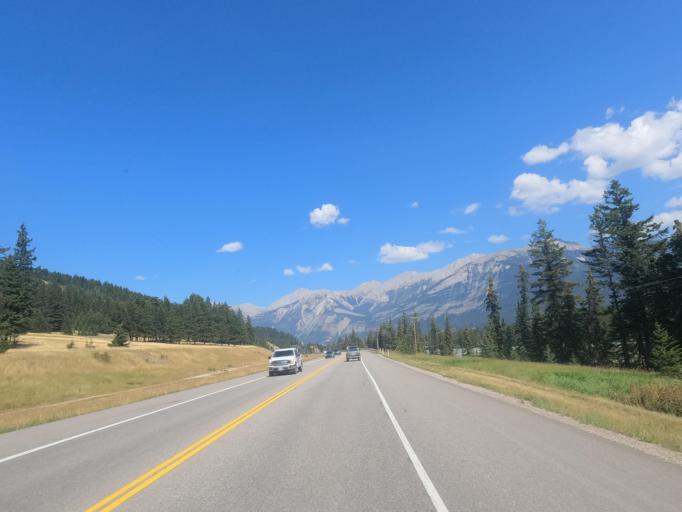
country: CA
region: Alberta
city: Jasper Park Lodge
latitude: 52.9056
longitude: -118.0638
